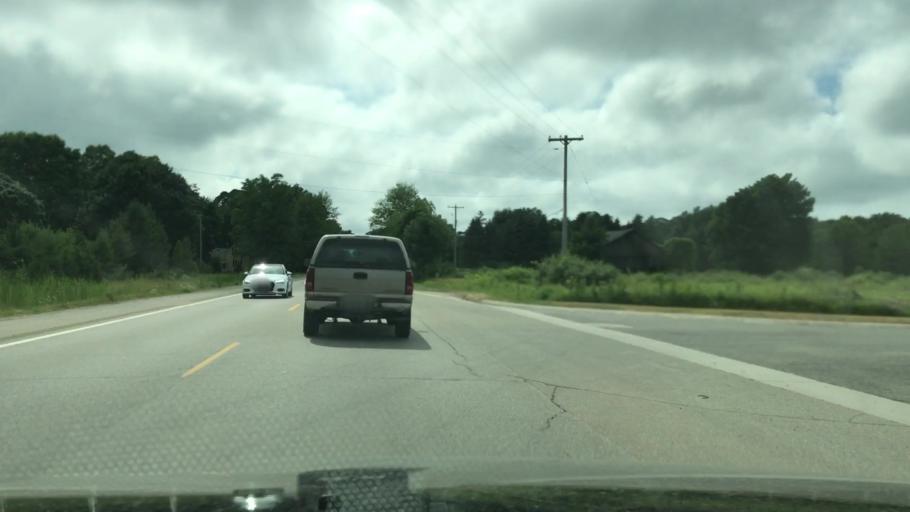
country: US
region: Michigan
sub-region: Muskegon County
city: Fruitport
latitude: 43.0742
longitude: -86.1038
